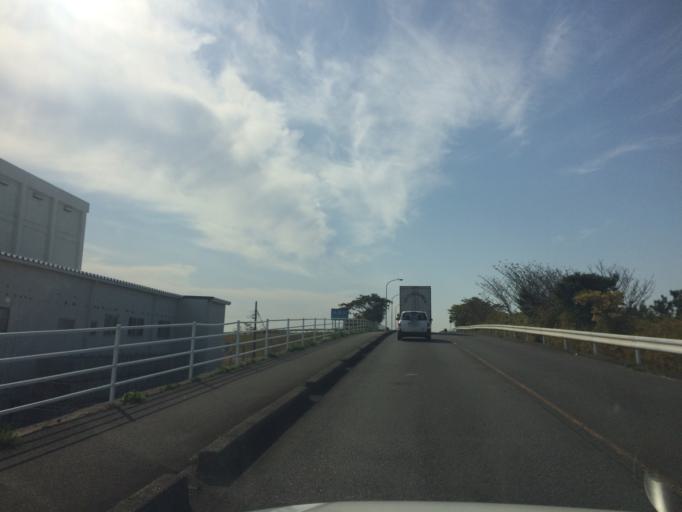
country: JP
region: Shizuoka
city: Fujieda
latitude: 34.7821
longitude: 138.2854
